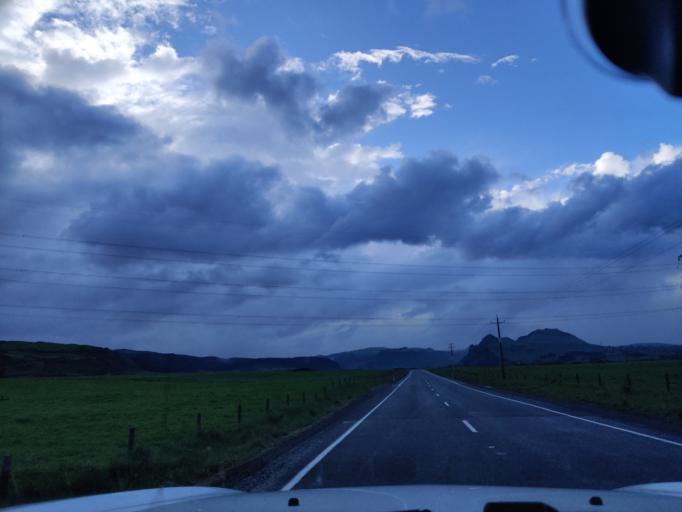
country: NZ
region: Waikato
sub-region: South Waikato District
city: Tokoroa
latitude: -38.3965
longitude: 175.7858
